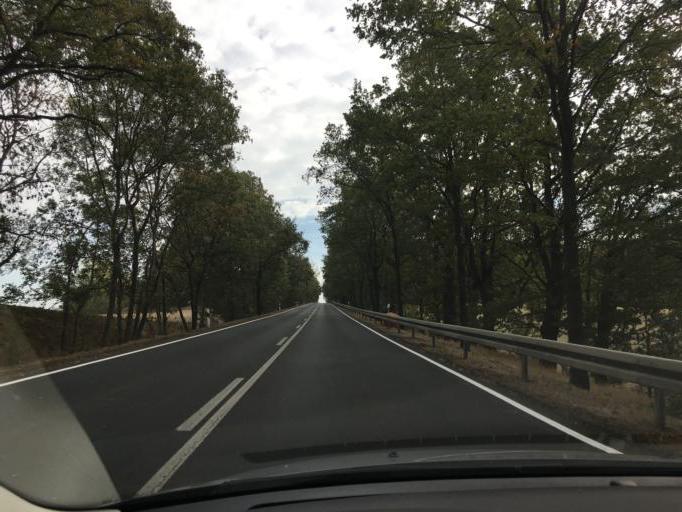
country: DE
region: Saxony
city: Oschatz
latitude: 51.2855
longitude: 13.1563
